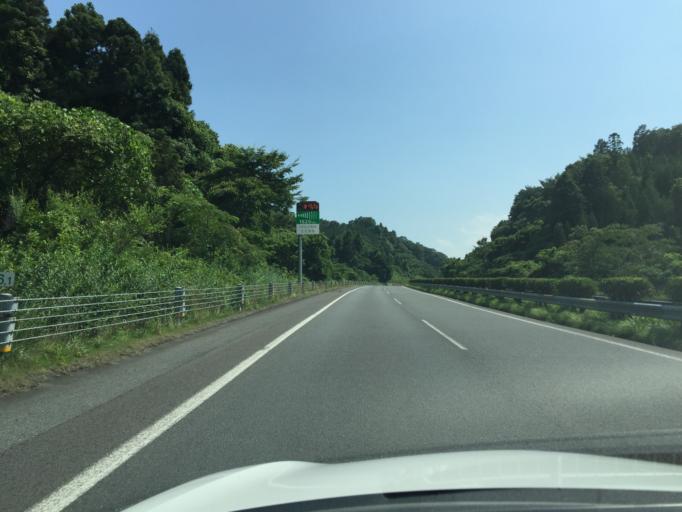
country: JP
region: Fukushima
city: Iwaki
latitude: 36.9938
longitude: 140.8059
